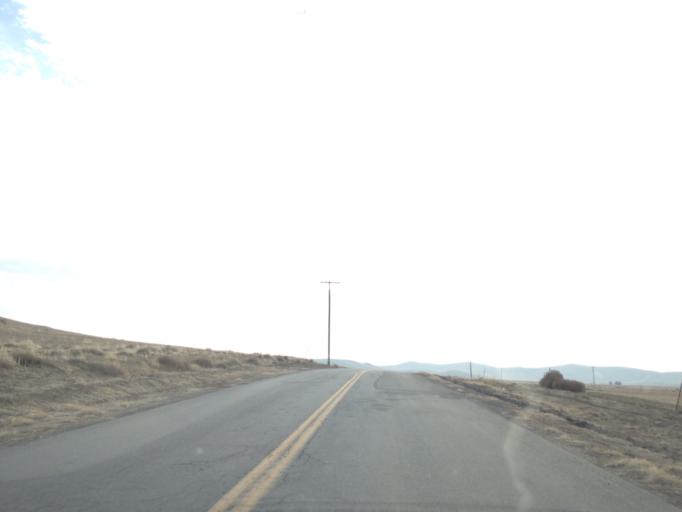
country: US
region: California
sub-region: Kings County
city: Kettleman City
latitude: 35.7331
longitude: -119.9750
